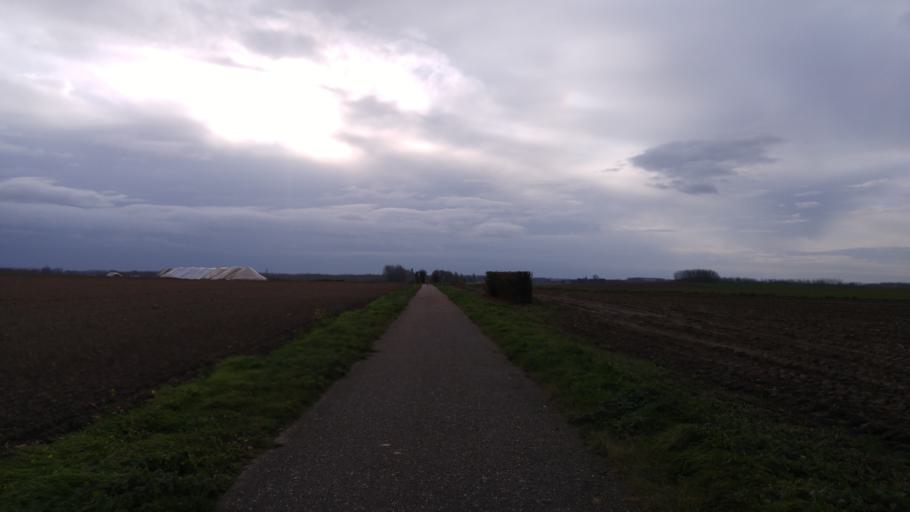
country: BE
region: Wallonia
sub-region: Province du Brabant Wallon
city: Ramillies
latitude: 50.6315
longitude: 4.8972
